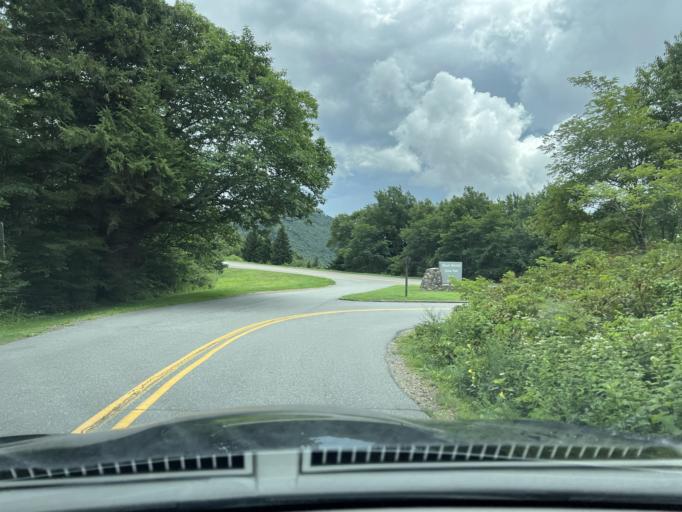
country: US
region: North Carolina
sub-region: Buncombe County
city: Black Mountain
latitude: 35.7184
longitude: -82.2796
